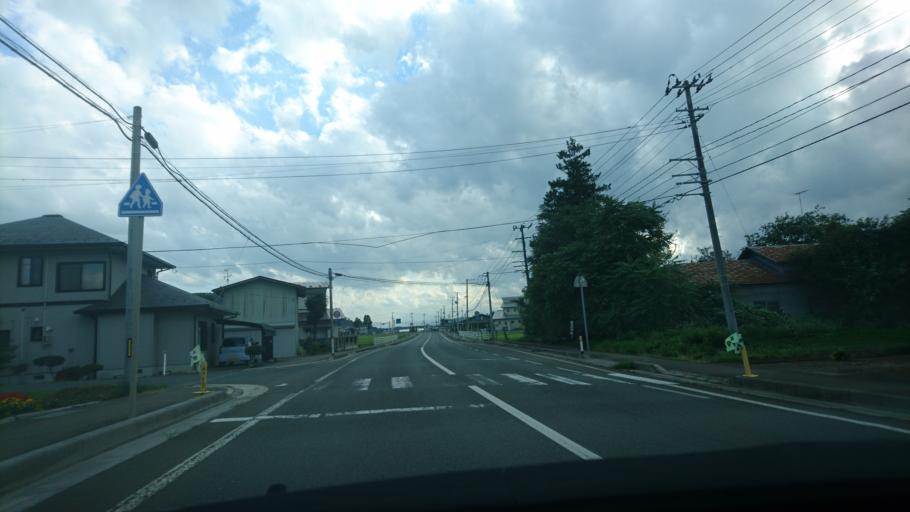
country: JP
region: Iwate
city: Kitakami
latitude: 39.2864
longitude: 141.1388
